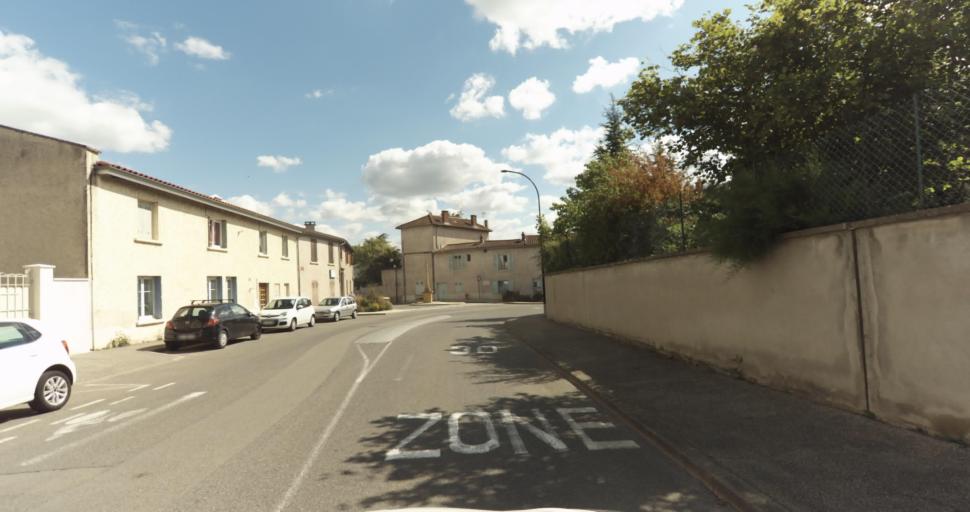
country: FR
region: Rhone-Alpes
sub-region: Departement du Rhone
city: Chaponost
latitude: 45.7126
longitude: 4.7494
